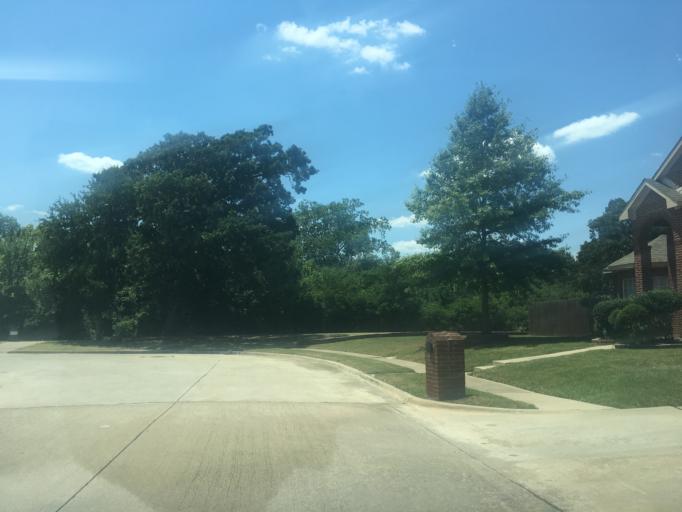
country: US
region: Texas
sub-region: Denton County
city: Lewisville
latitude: 33.0263
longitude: -97.0006
